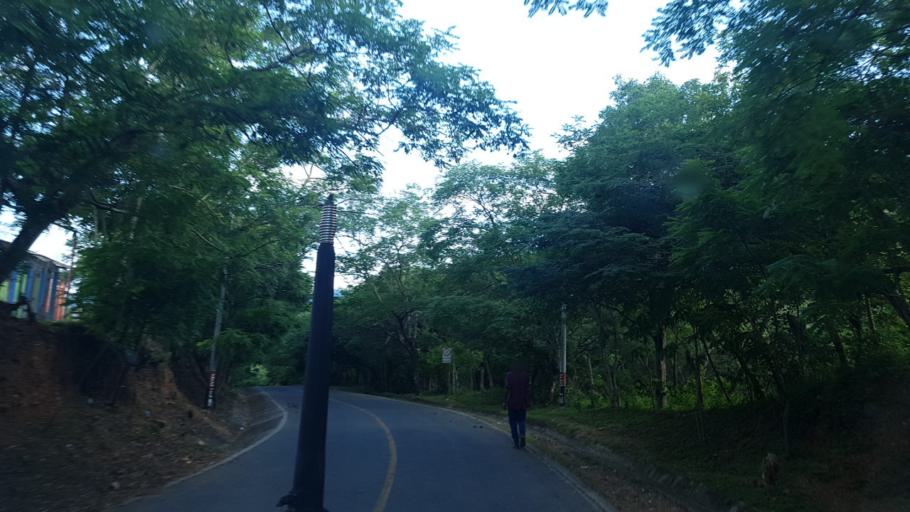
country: NI
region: Nueva Segovia
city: Ocotal
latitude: 13.6496
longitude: -86.6092
